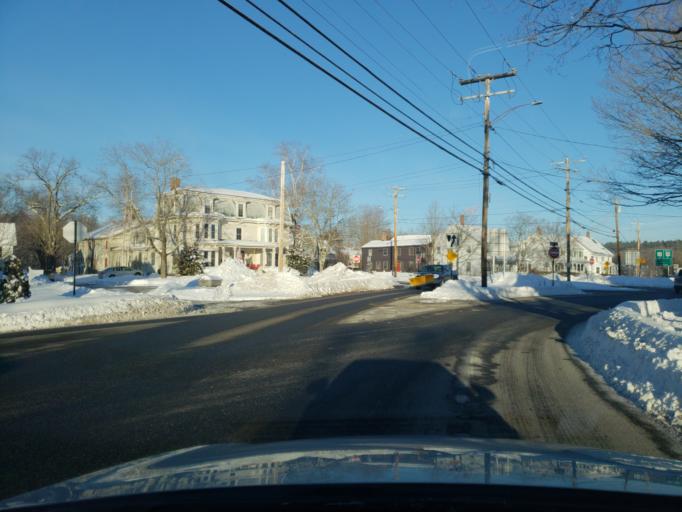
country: US
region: New Hampshire
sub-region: Hillsborough County
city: Goffstown
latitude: 43.0160
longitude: -71.5979
